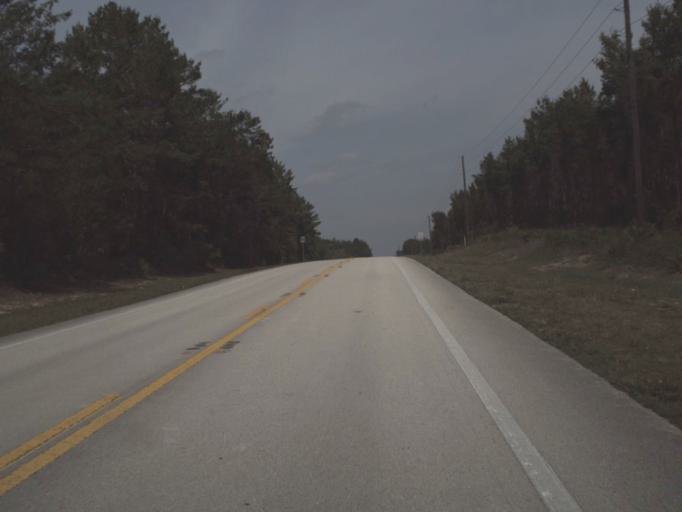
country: US
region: Florida
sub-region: Putnam County
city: Crescent City
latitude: 29.3161
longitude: -81.6940
